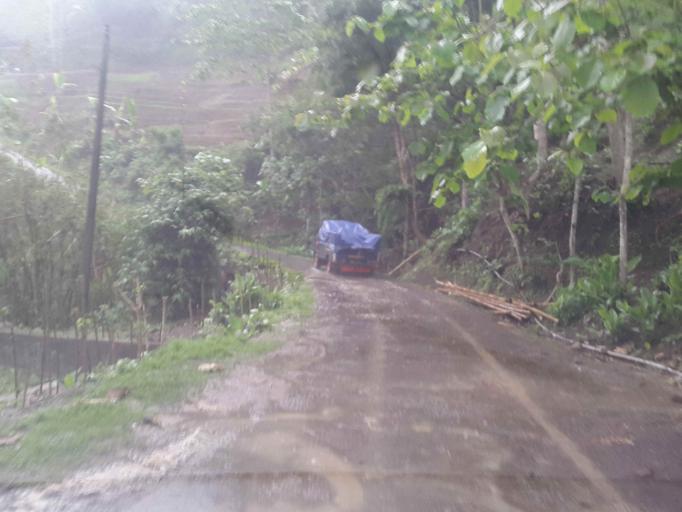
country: ID
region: Central Java
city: Bantarmangu
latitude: -7.3379
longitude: 108.8672
